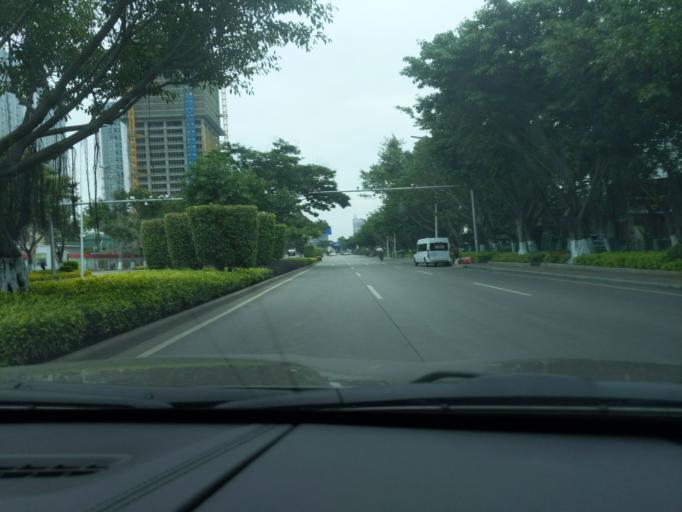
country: CN
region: Fujian
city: Liuwudian
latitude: 24.4879
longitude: 118.1626
